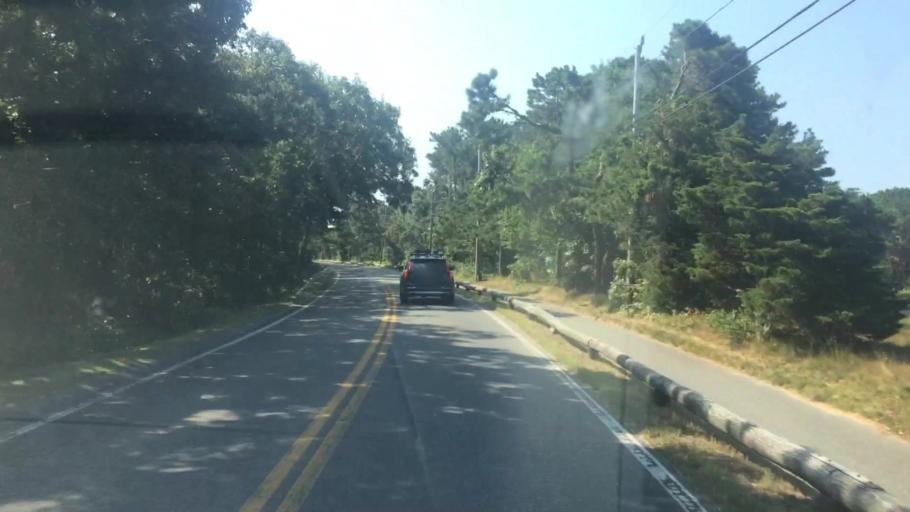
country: US
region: Massachusetts
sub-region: Dukes County
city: Oak Bluffs
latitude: 41.4381
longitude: -70.5570
